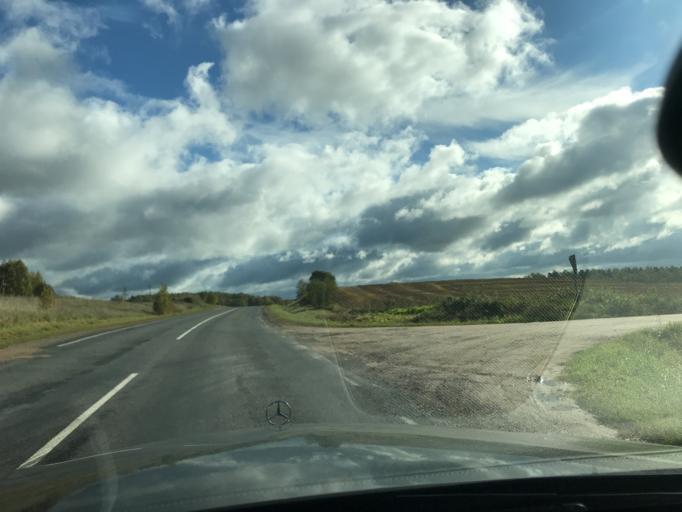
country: EE
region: Tartu
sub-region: Elva linn
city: Elva
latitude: 58.0096
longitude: 26.2439
